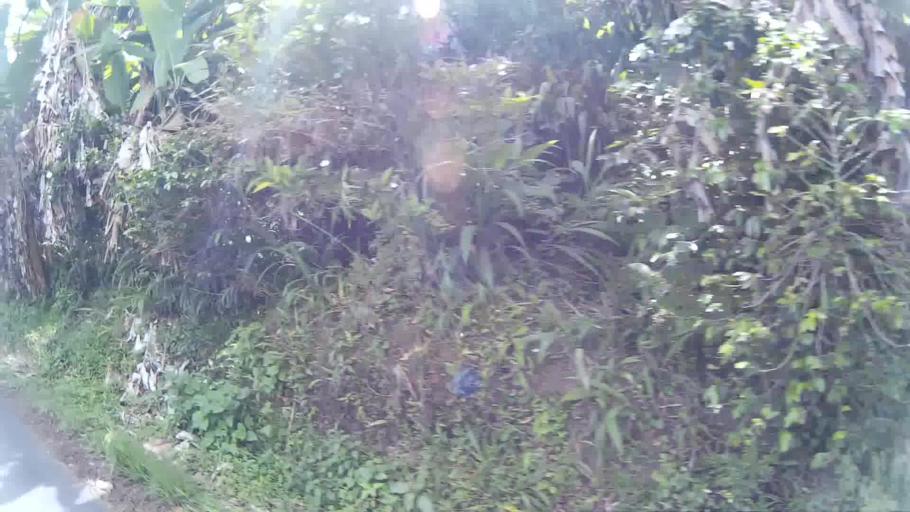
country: CO
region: Risaralda
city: Marsella
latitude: 4.8975
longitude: -75.7461
